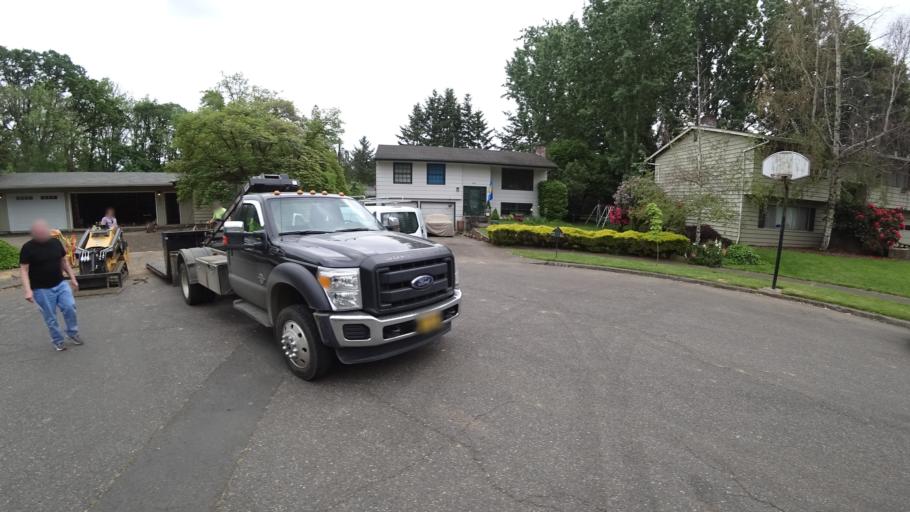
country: US
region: Oregon
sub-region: Washington County
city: Raleigh Hills
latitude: 45.4703
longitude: -122.7791
